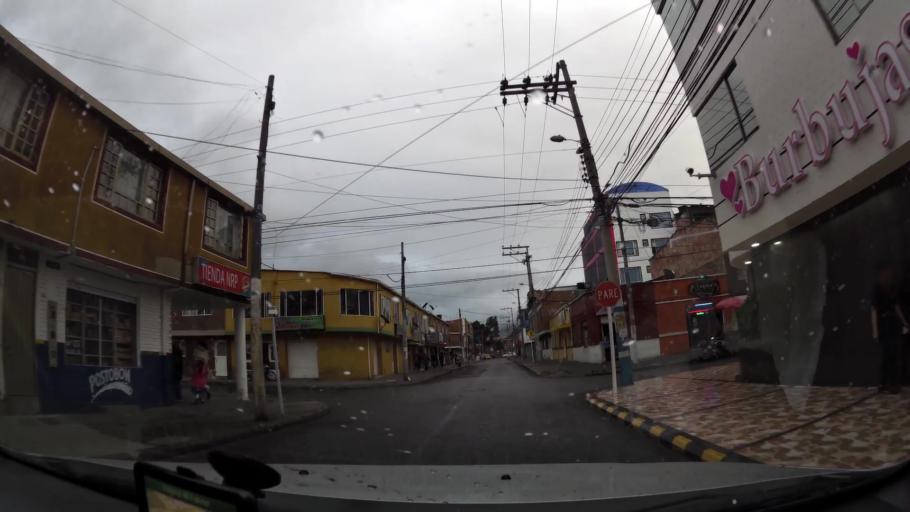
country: CO
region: Bogota D.C.
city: Bogota
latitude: 4.5919
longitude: -74.1371
